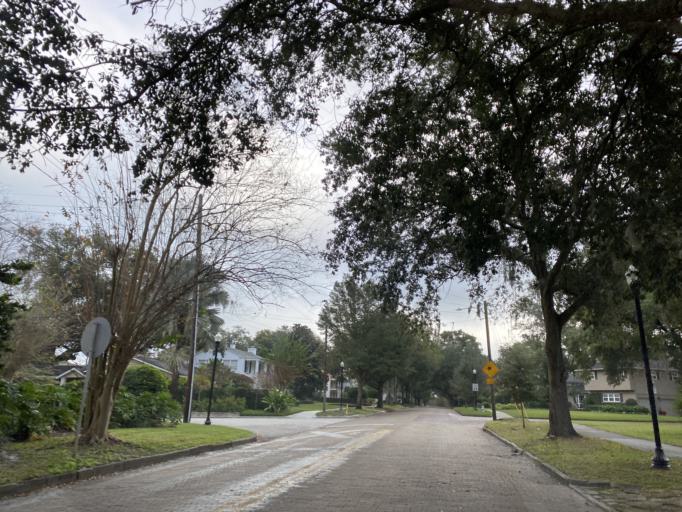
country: US
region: Florida
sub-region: Orange County
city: Orlando
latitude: 28.5601
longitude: -81.3970
